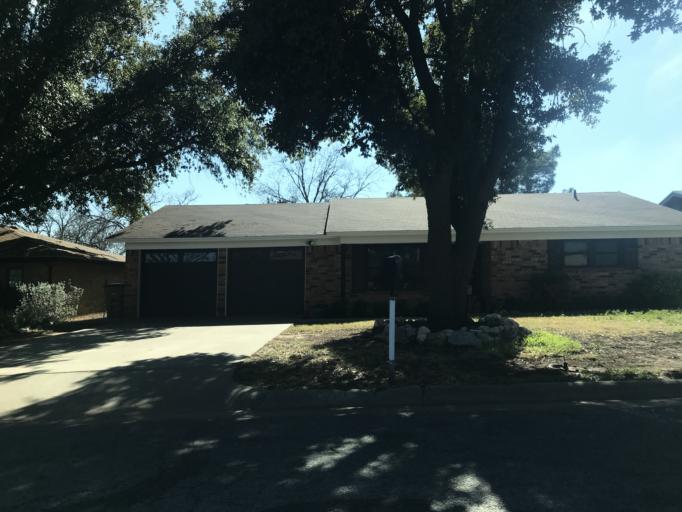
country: US
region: Texas
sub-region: Tom Green County
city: San Angelo
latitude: 31.4300
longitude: -100.4893
